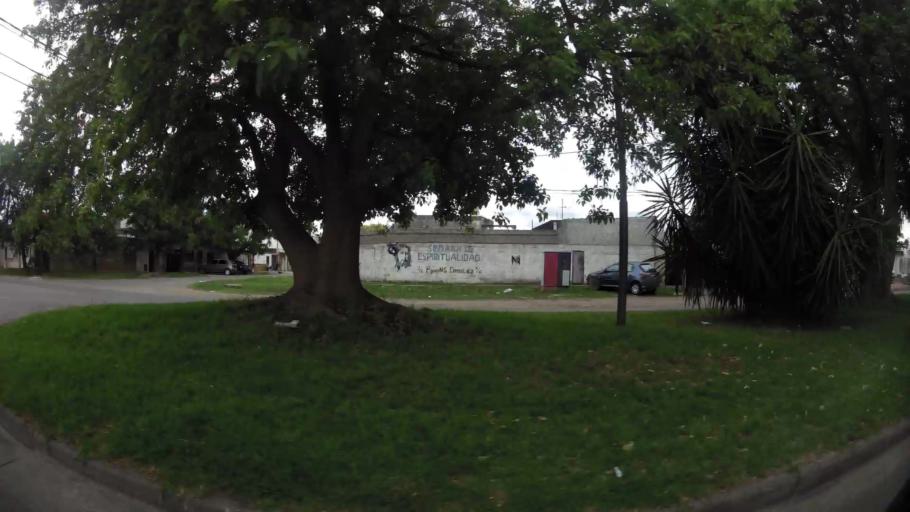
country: AR
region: Santa Fe
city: Gobernador Galvez
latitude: -33.0005
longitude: -60.6778
